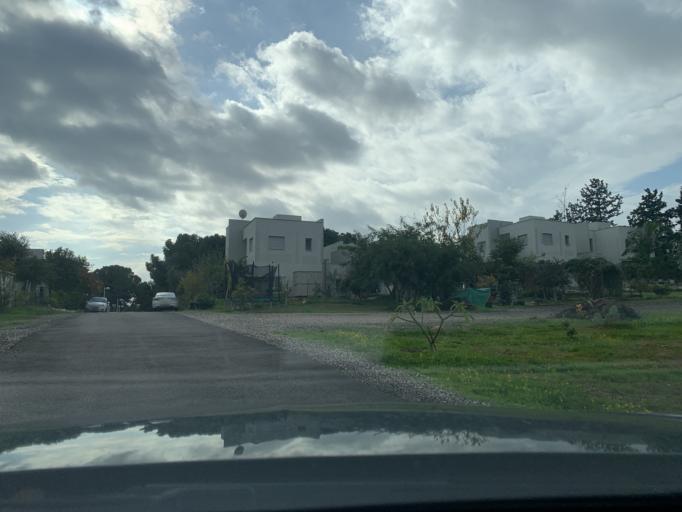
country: PS
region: West Bank
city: Qalqilyah
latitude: 32.2008
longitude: 34.9495
